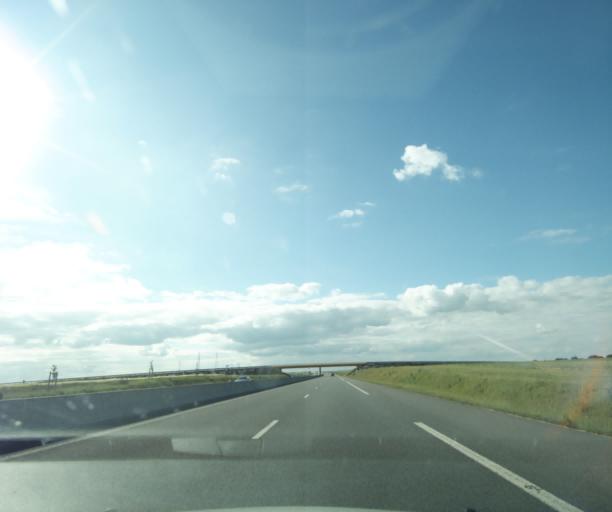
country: FR
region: Centre
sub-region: Departement d'Eure-et-Loir
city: Sours
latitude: 48.3457
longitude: 1.6294
